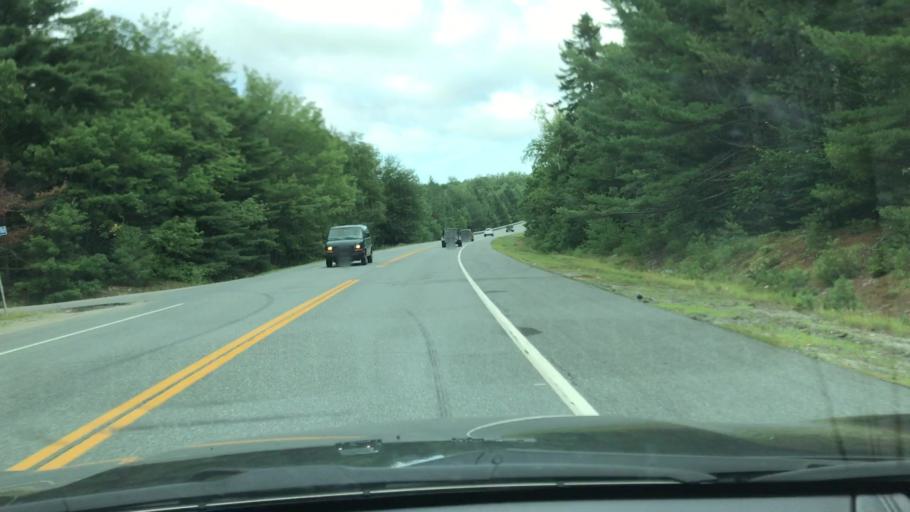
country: US
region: Maine
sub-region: Hancock County
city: Surry
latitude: 44.5569
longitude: -68.5462
